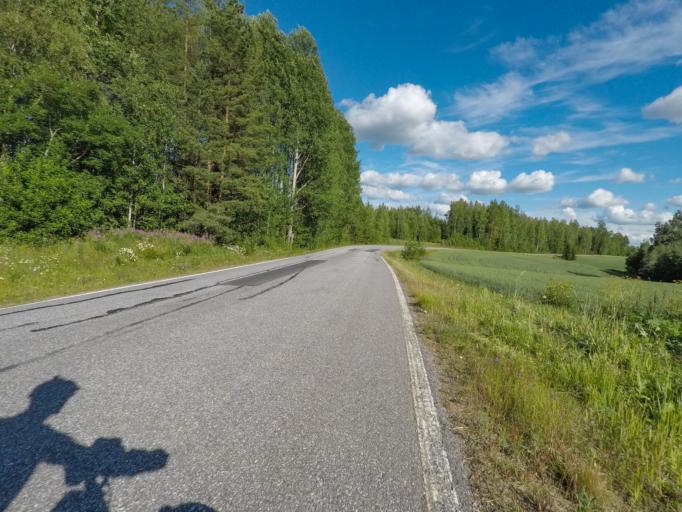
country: FI
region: South Karelia
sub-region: Imatra
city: Imatra
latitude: 61.1346
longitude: 28.6582
